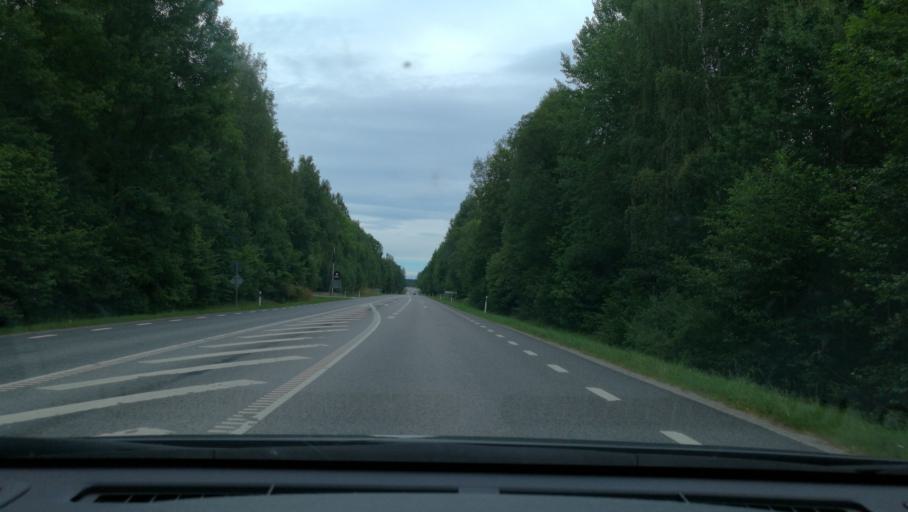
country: SE
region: Soedermanland
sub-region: Katrineholms Kommun
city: Katrineholm
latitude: 58.9694
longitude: 16.2000
